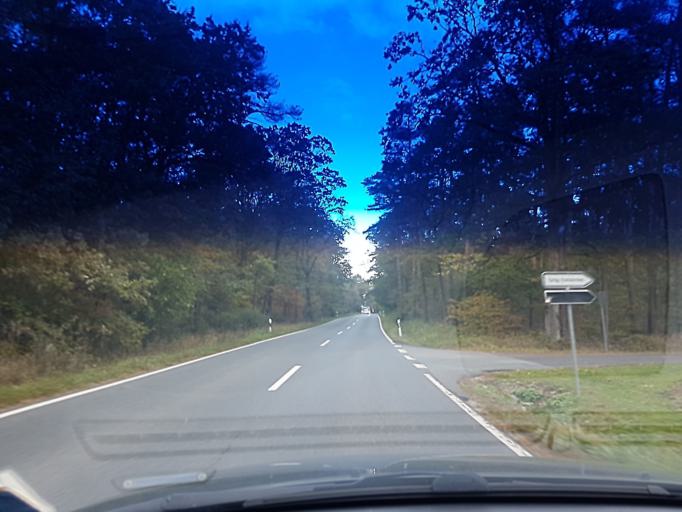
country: DE
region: Bavaria
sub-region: Regierungsbezirk Mittelfranken
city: Hochstadt an der Aisch
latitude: 49.7227
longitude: 10.8179
